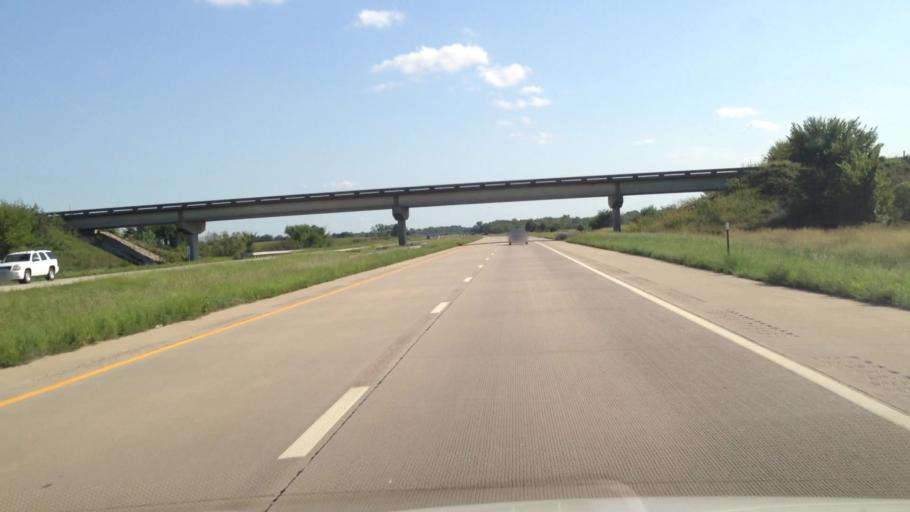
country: US
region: Kansas
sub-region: Bourbon County
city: Fort Scott
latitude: 37.9223
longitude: -94.7046
